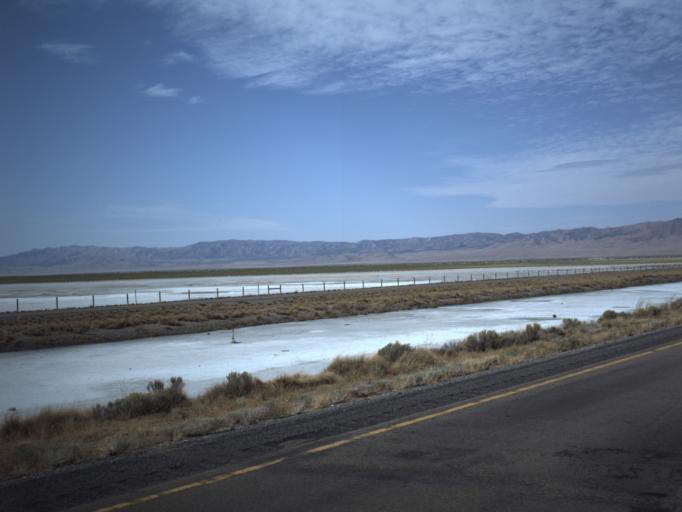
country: US
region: Utah
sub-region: Tooele County
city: Grantsville
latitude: 40.7512
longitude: -112.7036
